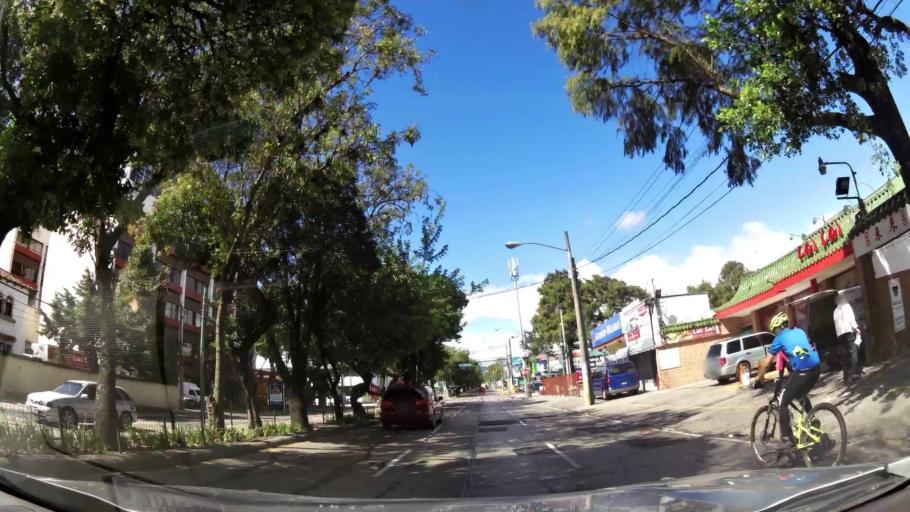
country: GT
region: Guatemala
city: Guatemala City
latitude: 14.6017
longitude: -90.5213
